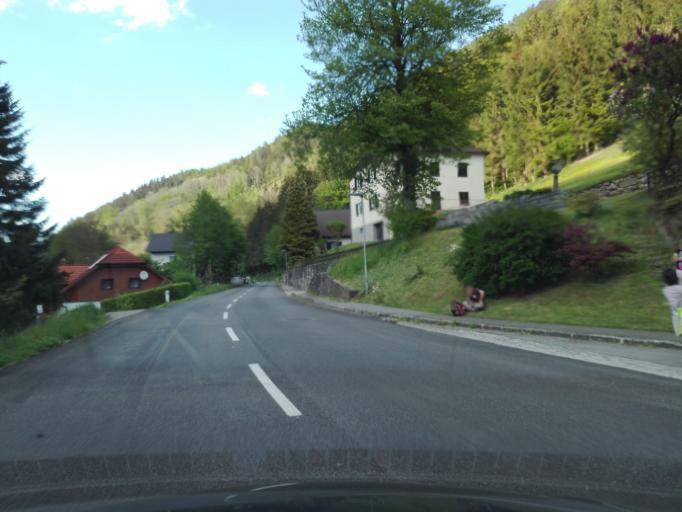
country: AT
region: Upper Austria
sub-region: Politischer Bezirk Rohrbach
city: Atzesberg
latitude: 48.4538
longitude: 13.9212
